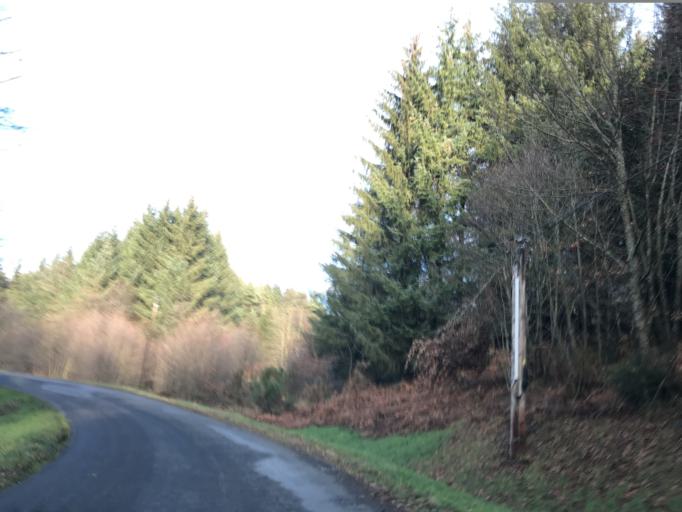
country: FR
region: Auvergne
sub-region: Departement du Puy-de-Dome
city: Celles-sur-Durolle
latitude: 45.7794
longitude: 3.6717
